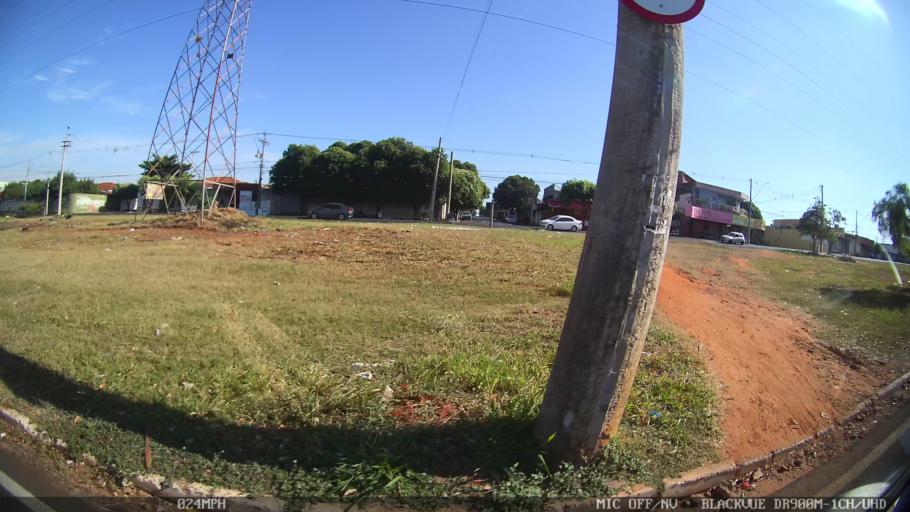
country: BR
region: Sao Paulo
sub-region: Sao Jose Do Rio Preto
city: Sao Jose do Rio Preto
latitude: -20.7825
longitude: -49.4066
